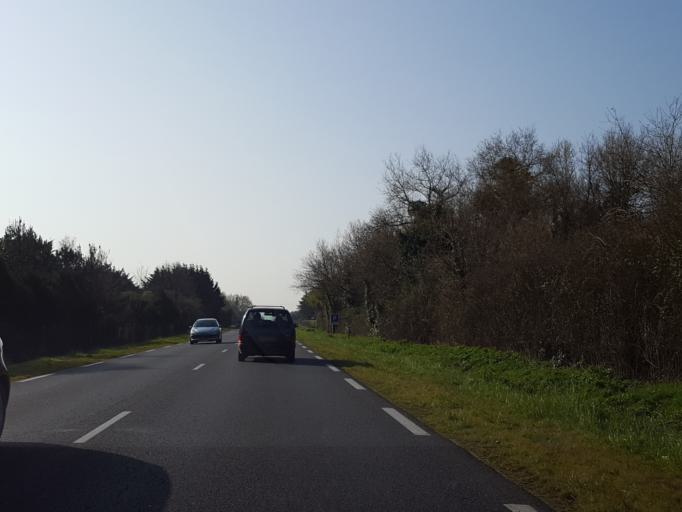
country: FR
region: Pays de la Loire
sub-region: Departement de la Loire-Atlantique
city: Geneston
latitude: 47.0854
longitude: -1.5271
